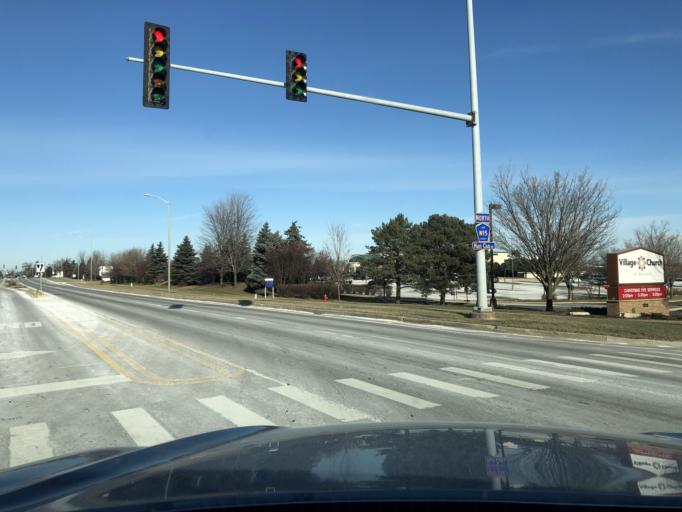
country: US
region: Illinois
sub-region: Lake County
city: Grandwood Park
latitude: 42.3792
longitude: -87.9634
